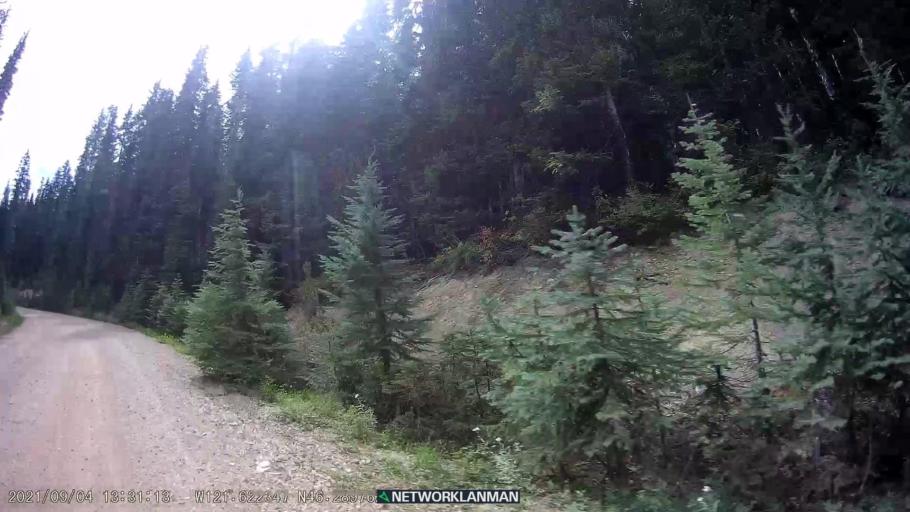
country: US
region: Washington
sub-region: Klickitat County
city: White Salmon
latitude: 46.2897
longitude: -121.6223
